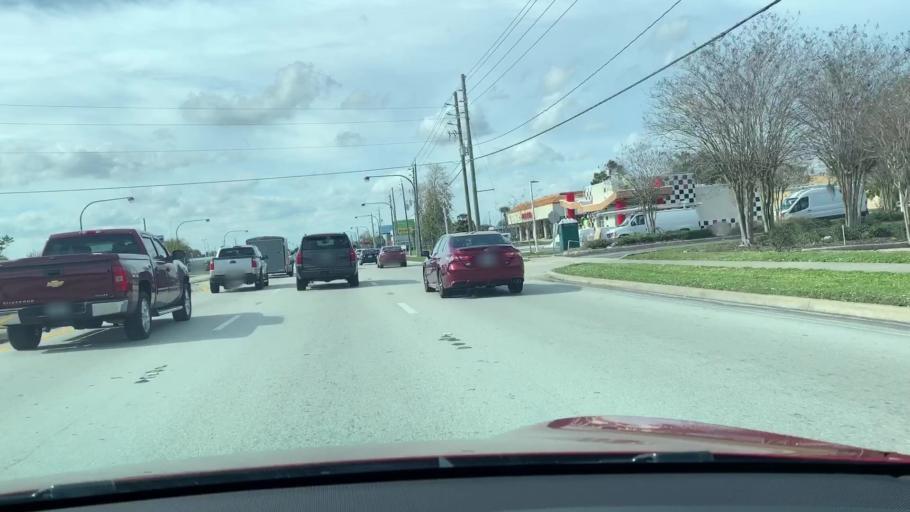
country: US
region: Florida
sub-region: Osceola County
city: Kissimmee
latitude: 28.3046
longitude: -81.4326
